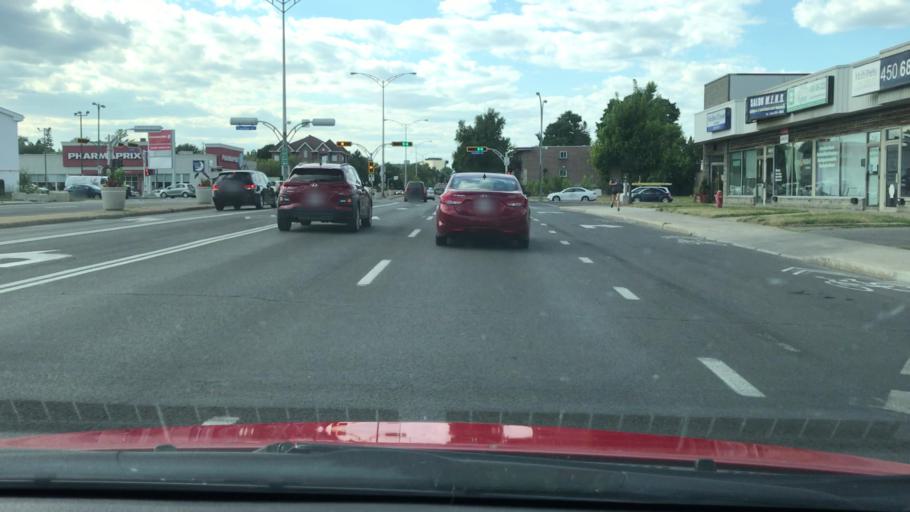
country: CA
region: Quebec
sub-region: Laval
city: Laval
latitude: 45.5386
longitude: -73.7333
